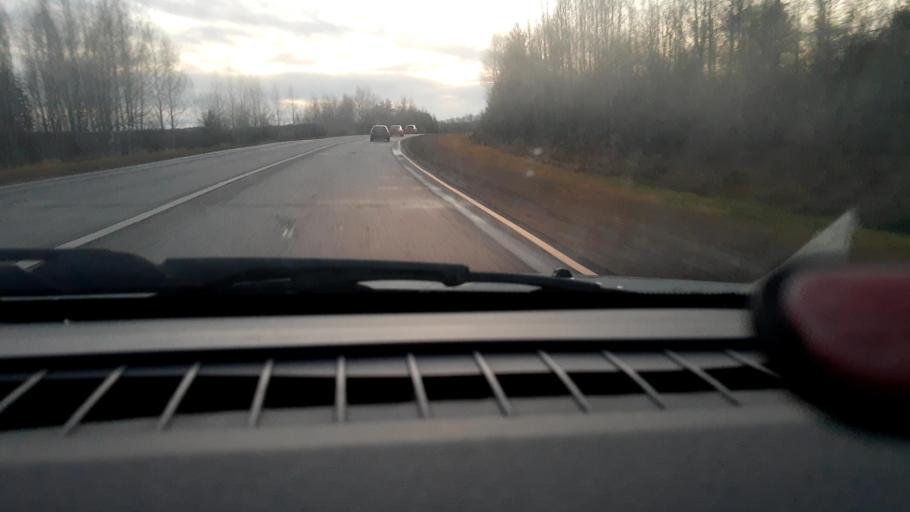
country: RU
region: Nizjnij Novgorod
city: Vladimirskoye
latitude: 56.9601
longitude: 45.1049
